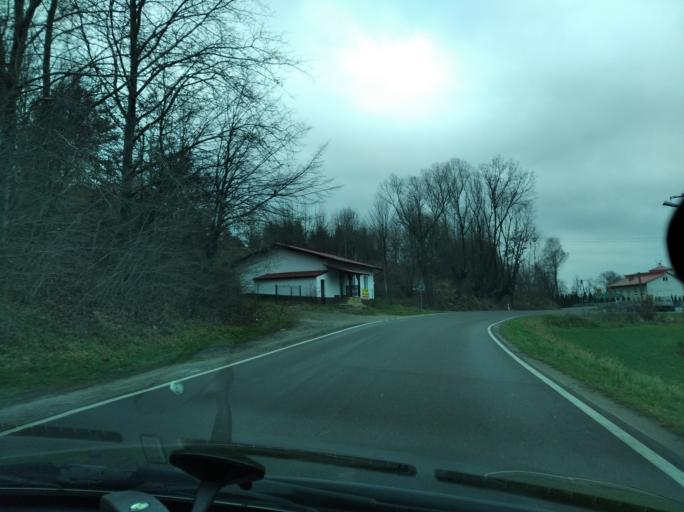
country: PL
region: Subcarpathian Voivodeship
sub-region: Powiat przeworski
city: Manasterz
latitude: 49.9270
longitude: 22.3361
